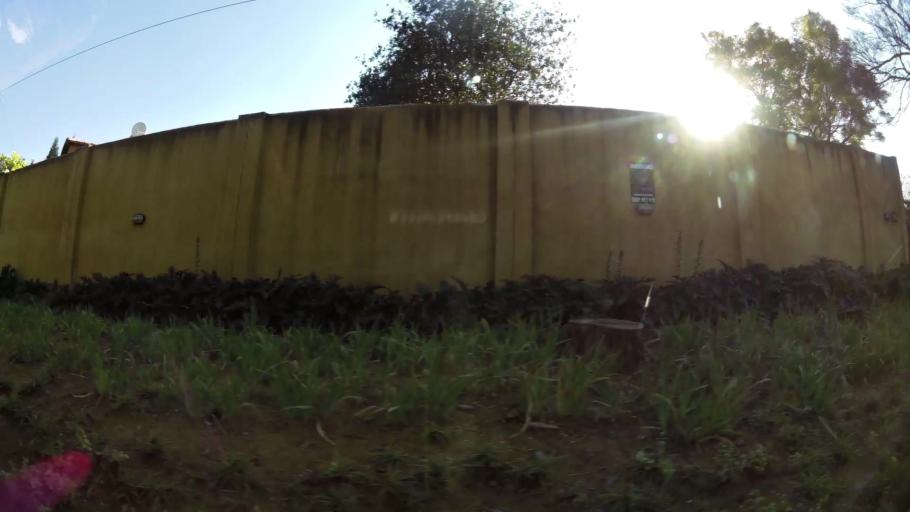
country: ZA
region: Gauteng
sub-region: City of Johannesburg Metropolitan Municipality
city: Modderfontein
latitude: -26.1089
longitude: 28.0709
